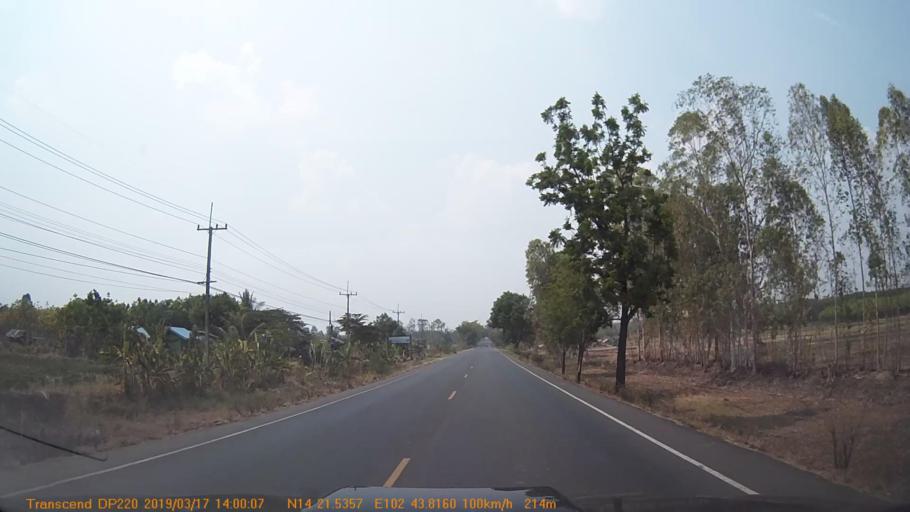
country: TH
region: Buriram
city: Non Din Daeng
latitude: 14.3592
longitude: 102.7300
